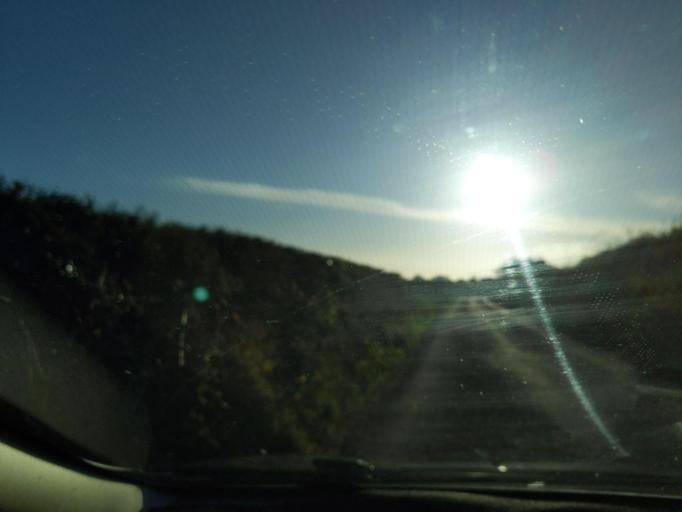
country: GB
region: England
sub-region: Plymouth
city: Plymstock
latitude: 50.3453
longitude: -4.1083
